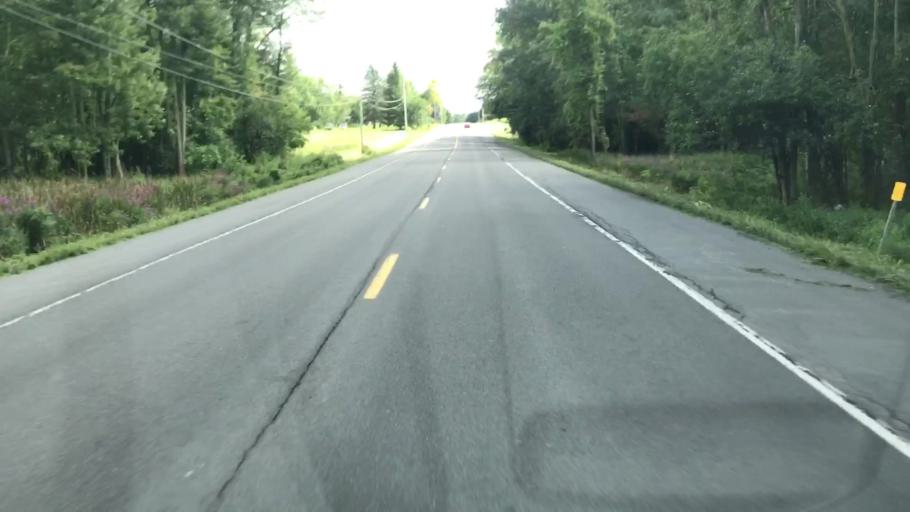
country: US
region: New York
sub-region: Onondaga County
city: Skaneateles
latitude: 42.9431
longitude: -76.4656
